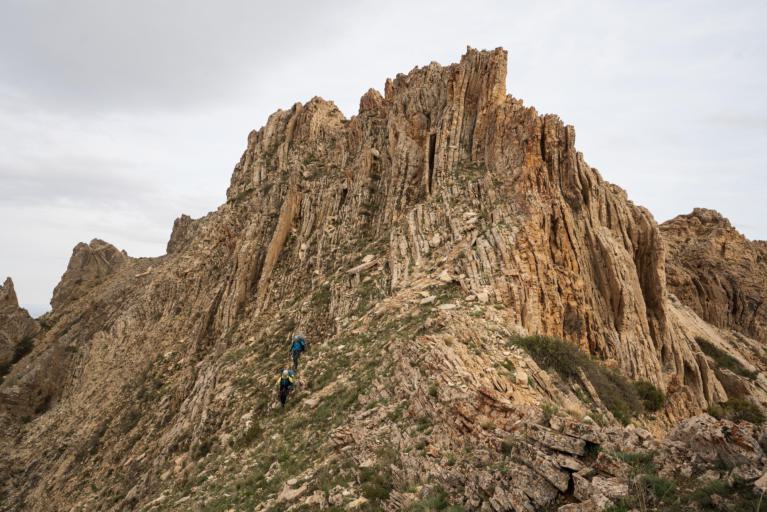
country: KZ
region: Ongtustik Qazaqstan
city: Ashchysay
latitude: 43.7570
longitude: 68.8147
